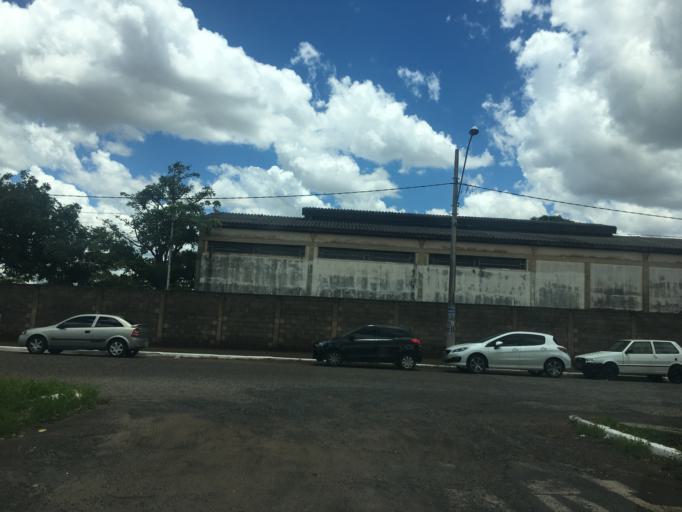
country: BR
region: Minas Gerais
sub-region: Uberlandia
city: Uberlandia
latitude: -18.9365
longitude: -48.3065
